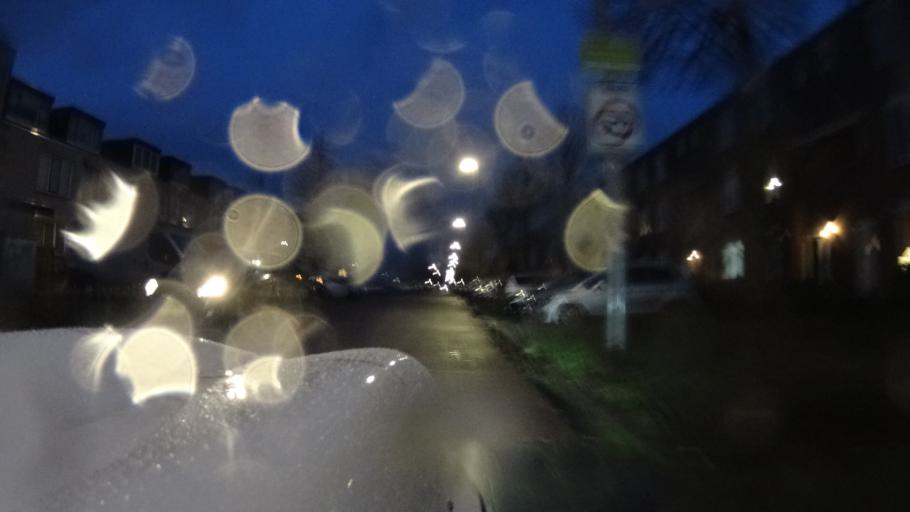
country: NL
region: South Holland
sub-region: Gemeente Rijnwoude
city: Benthuizen
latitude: 52.0719
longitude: 4.5205
